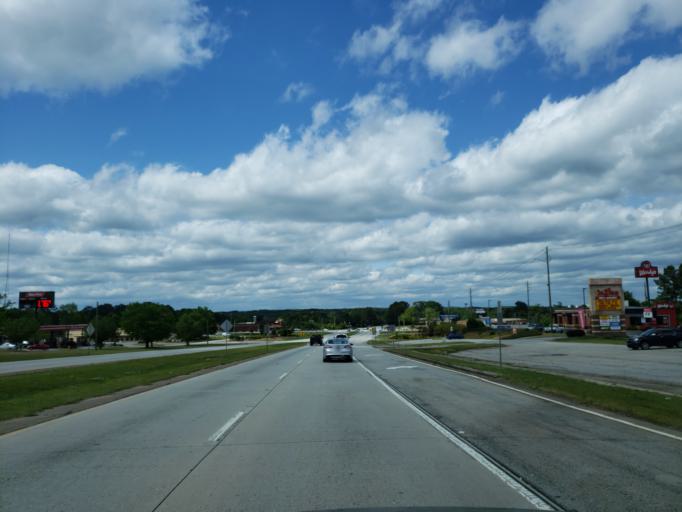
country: US
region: Georgia
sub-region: Carroll County
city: Villa Rica
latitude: 33.7266
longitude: -84.9397
